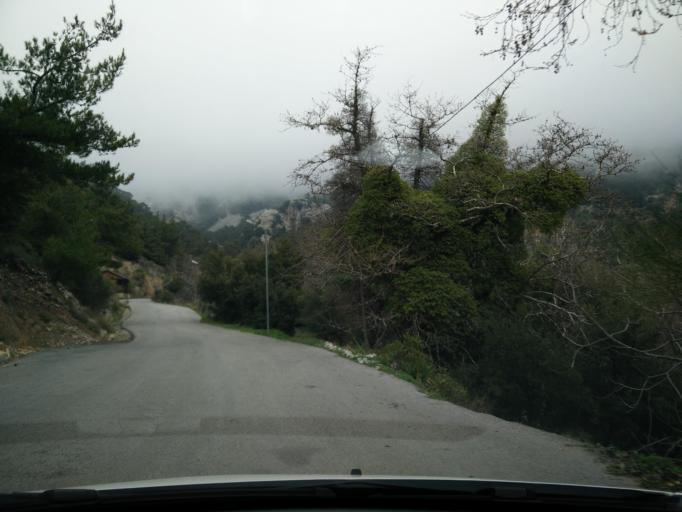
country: GR
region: Crete
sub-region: Nomos Lasithiou
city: Kritsa
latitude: 35.0485
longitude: 25.4893
